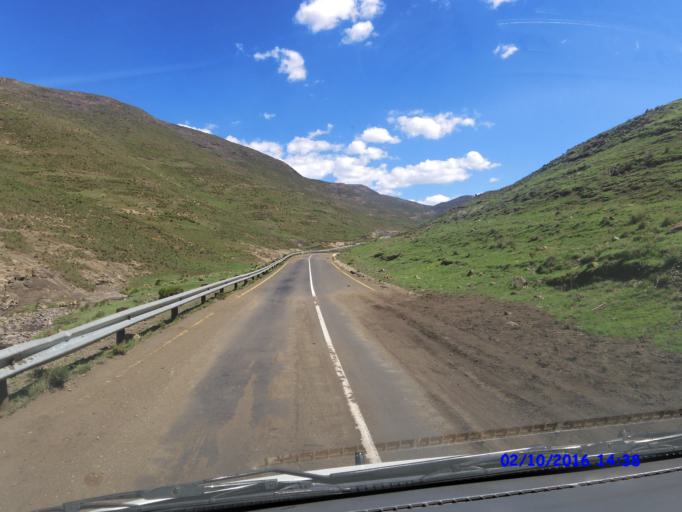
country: LS
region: Maseru
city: Nako
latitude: -29.5078
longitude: 28.0632
